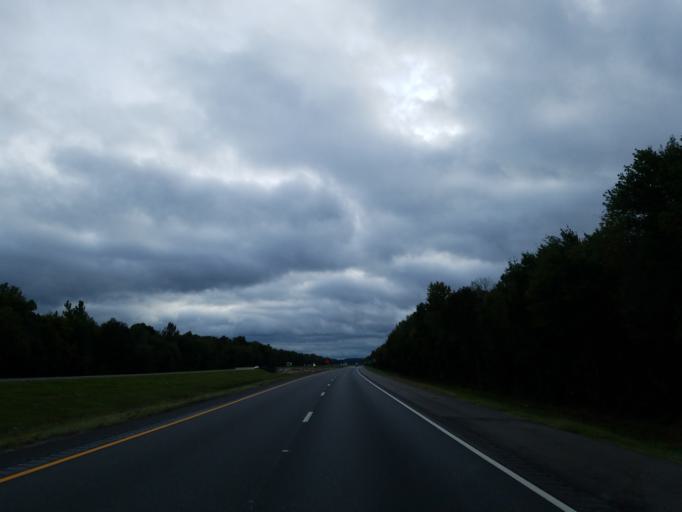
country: US
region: Alabama
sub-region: Hale County
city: Moundville
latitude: 33.1071
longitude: -87.6601
